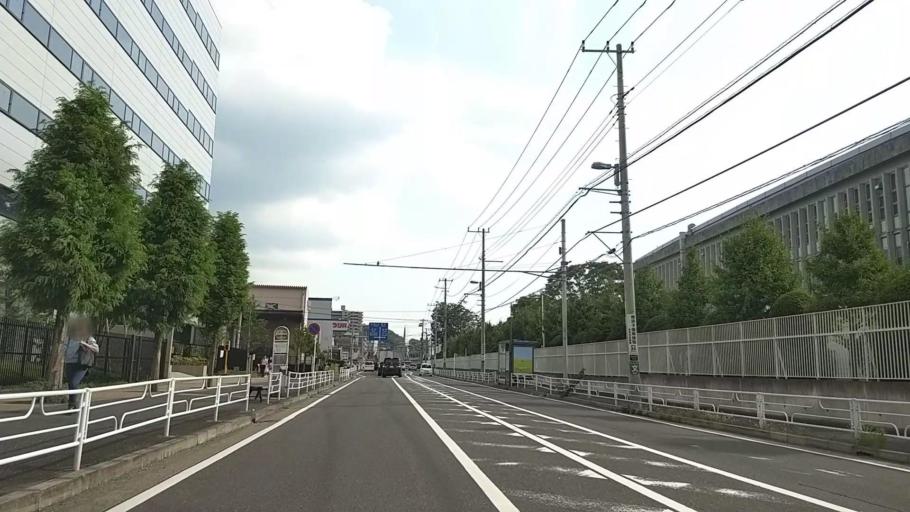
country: JP
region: Kanagawa
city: Yokohama
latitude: 35.5168
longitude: 139.5635
